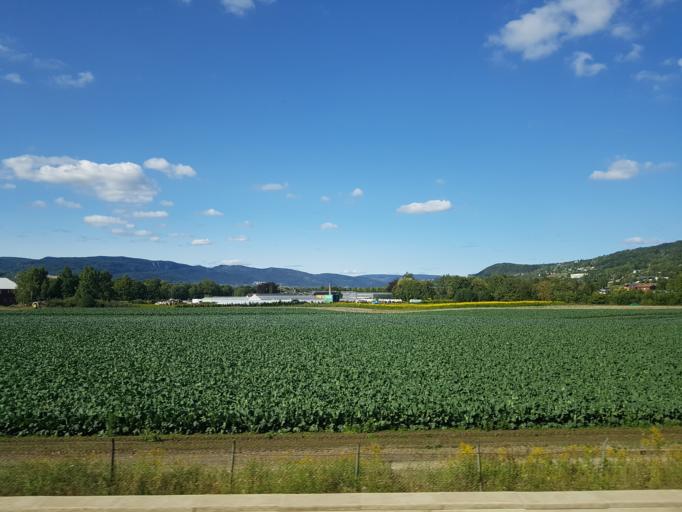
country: NO
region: Buskerud
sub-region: Lier
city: Lierbyen
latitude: 59.7613
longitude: 10.2827
